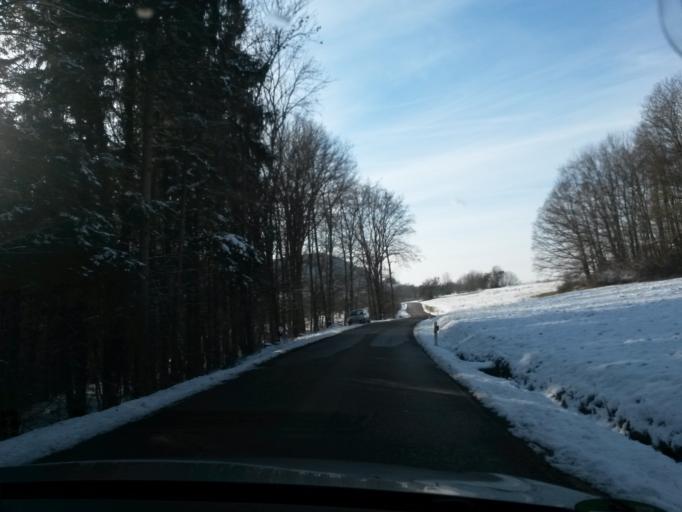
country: DE
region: Baden-Wuerttemberg
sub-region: Regierungsbezirk Stuttgart
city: Gingen an der Fils
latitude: 48.6535
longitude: 9.7577
